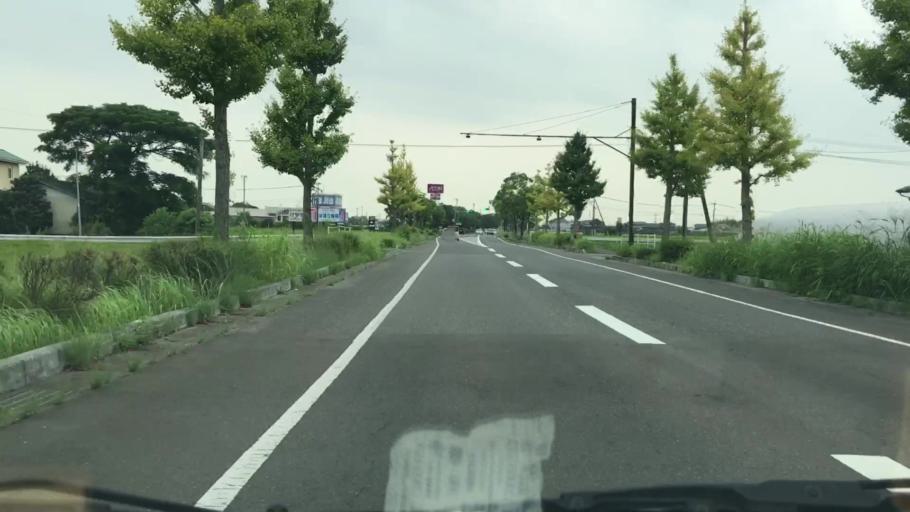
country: JP
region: Saga Prefecture
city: Saga-shi
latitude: 33.2254
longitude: 130.3063
